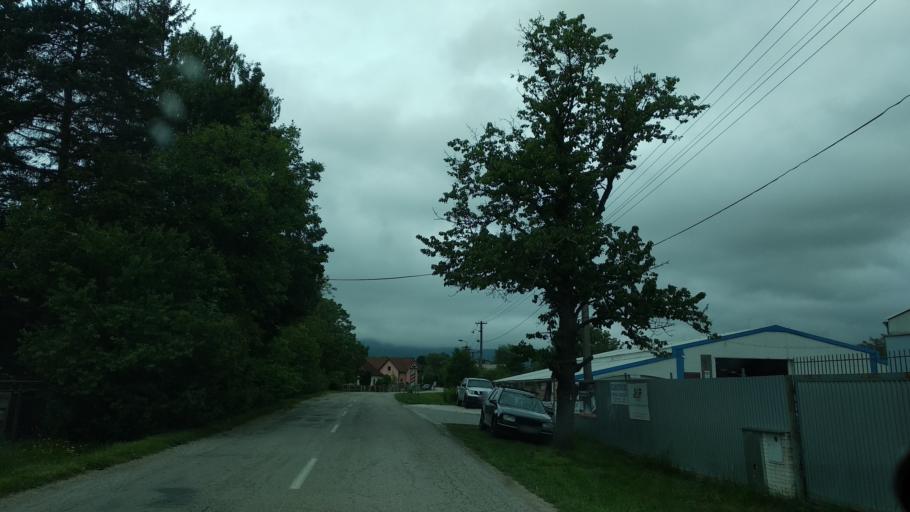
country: SK
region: Nitriansky
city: Trencianske Teplice
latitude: 48.7885
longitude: 18.1519
